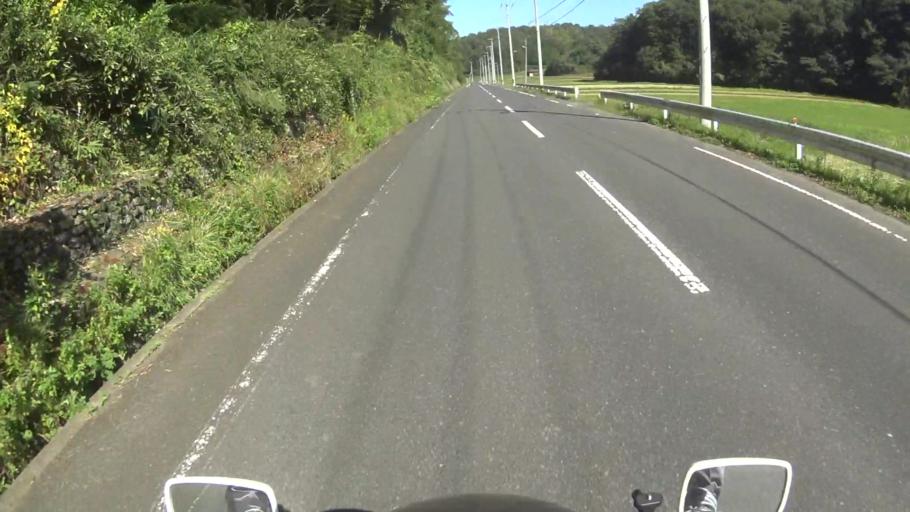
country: JP
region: Kyoto
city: Miyazu
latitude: 35.6621
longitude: 135.0595
